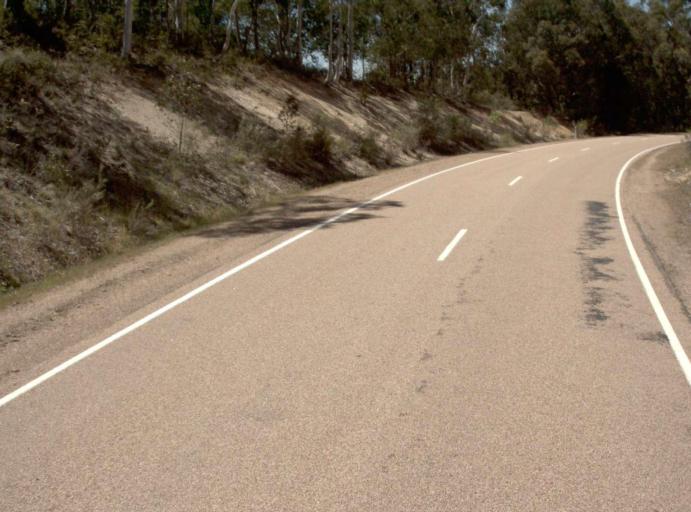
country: AU
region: Victoria
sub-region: East Gippsland
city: Lakes Entrance
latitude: -37.1472
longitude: 148.2507
